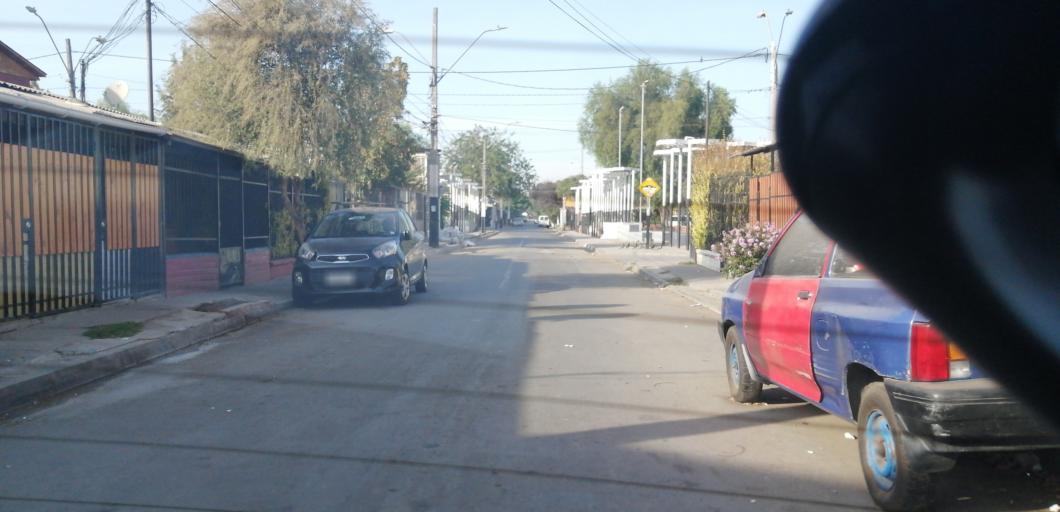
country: CL
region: Santiago Metropolitan
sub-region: Provincia de Santiago
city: Lo Prado
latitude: -33.4607
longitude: -70.7546
